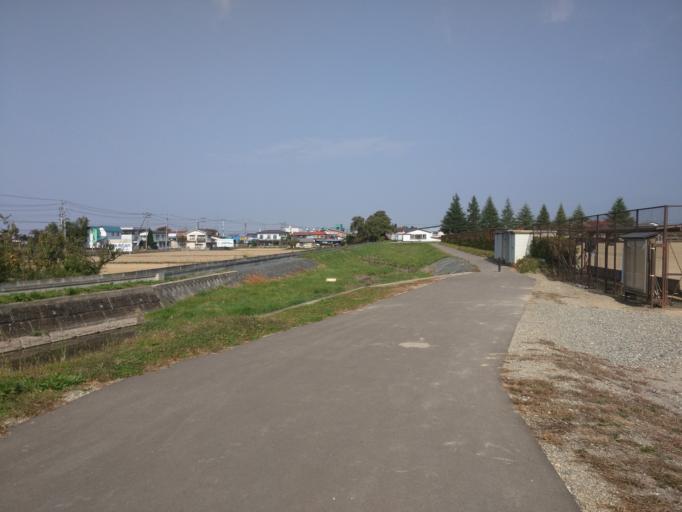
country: JP
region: Fukushima
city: Kitakata
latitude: 37.4620
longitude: 139.9229
